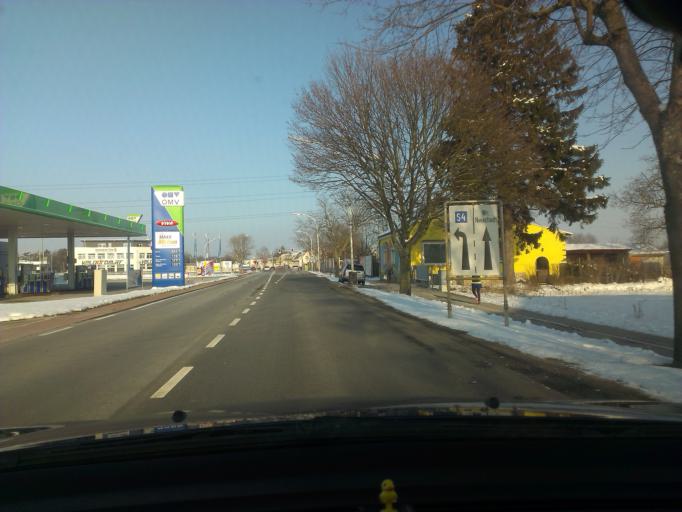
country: AT
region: Lower Austria
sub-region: Wiener Neustadt Stadt
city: Wiener Neustadt
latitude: 47.8047
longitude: 16.2685
